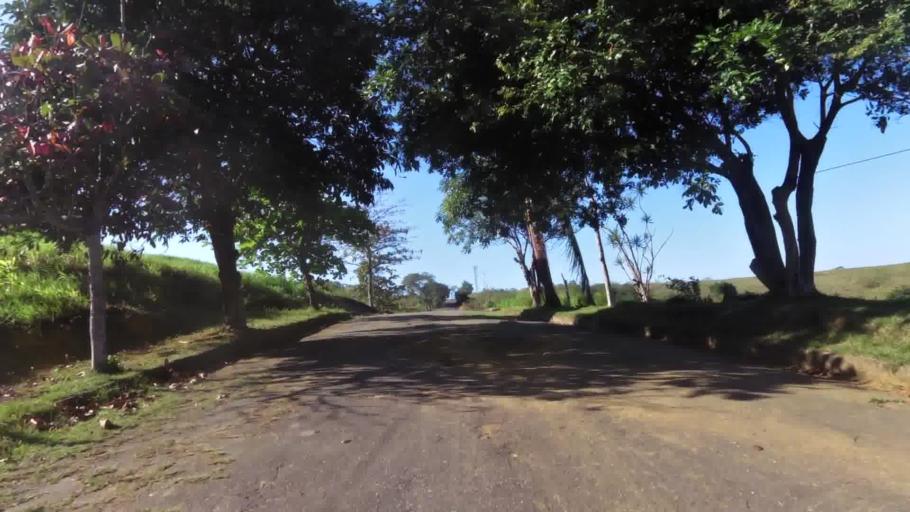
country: BR
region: Espirito Santo
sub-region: Guarapari
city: Guarapari
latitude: -20.7397
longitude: -40.5565
